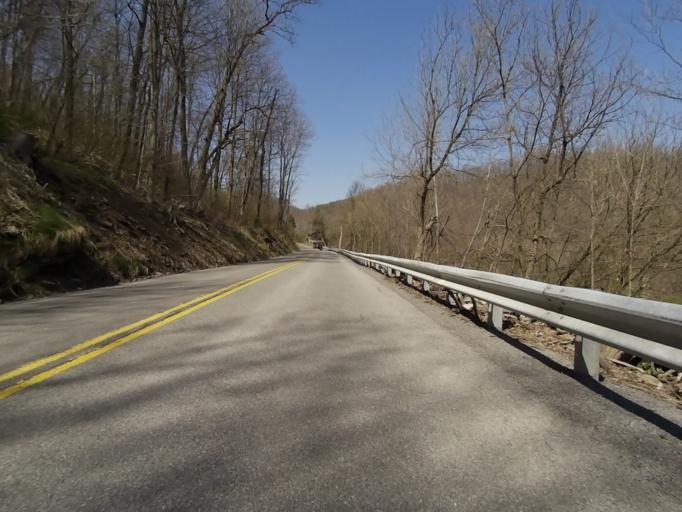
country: US
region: Pennsylvania
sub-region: Blair County
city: Tyrone
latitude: 40.6085
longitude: -78.1375
